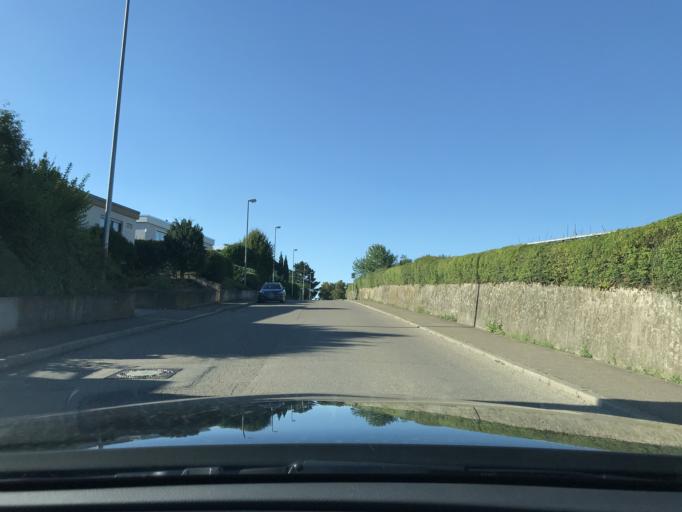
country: DE
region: Baden-Wuerttemberg
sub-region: Regierungsbezirk Stuttgart
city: Weinstadt-Endersbach
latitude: 48.7952
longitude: 9.3469
